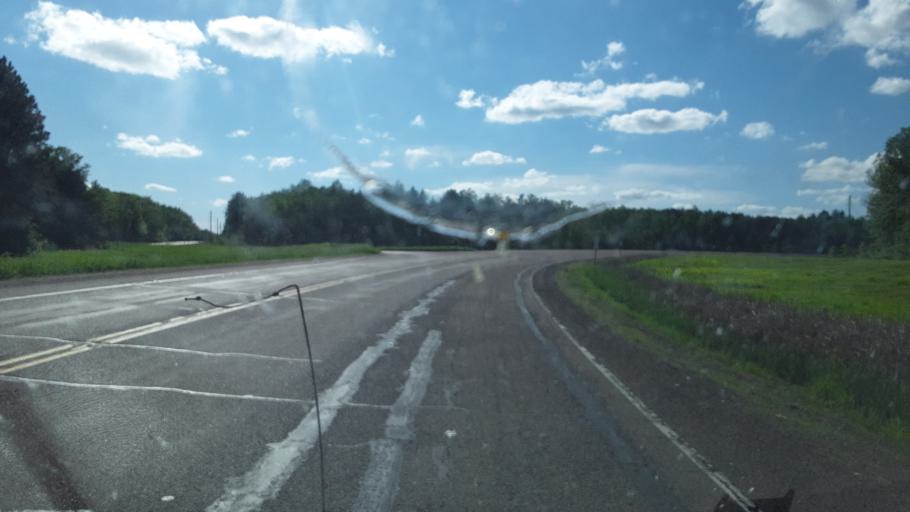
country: US
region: Wisconsin
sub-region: Wood County
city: Marshfield
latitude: 44.4538
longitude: -90.1773
